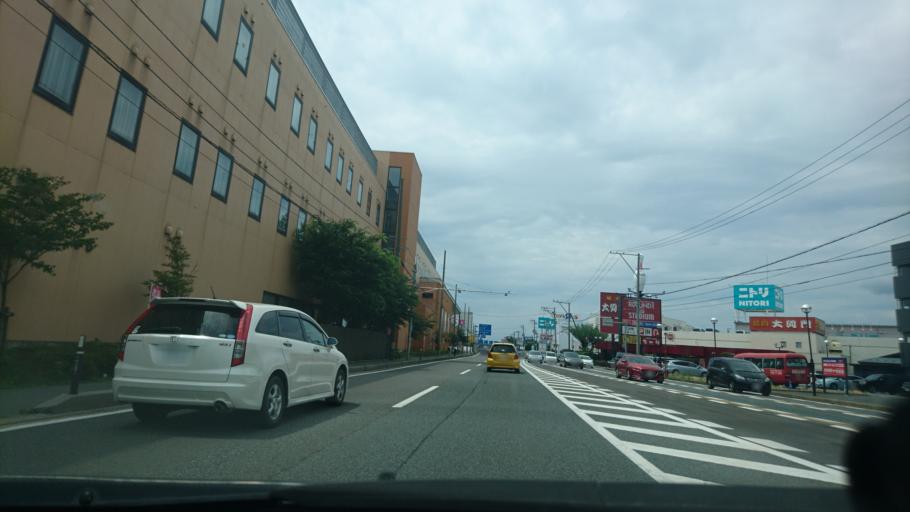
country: JP
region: Akita
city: Akita
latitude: 39.7012
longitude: 140.1097
